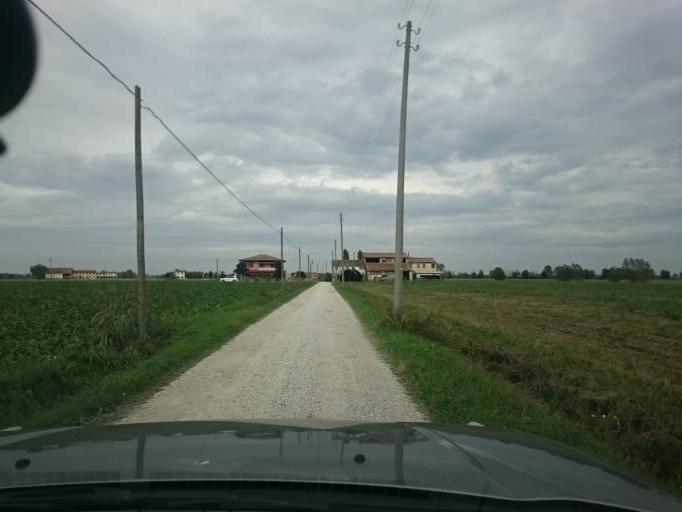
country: IT
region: Veneto
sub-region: Provincia di Padova
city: Correzzola
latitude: 45.2415
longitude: 12.0684
